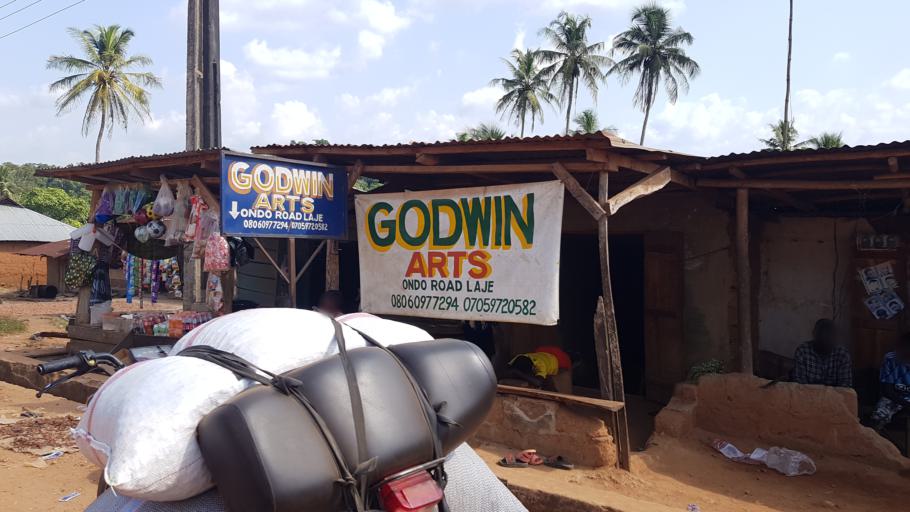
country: NG
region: Osun
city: Ifetedo
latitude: 7.0167
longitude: 4.6342
